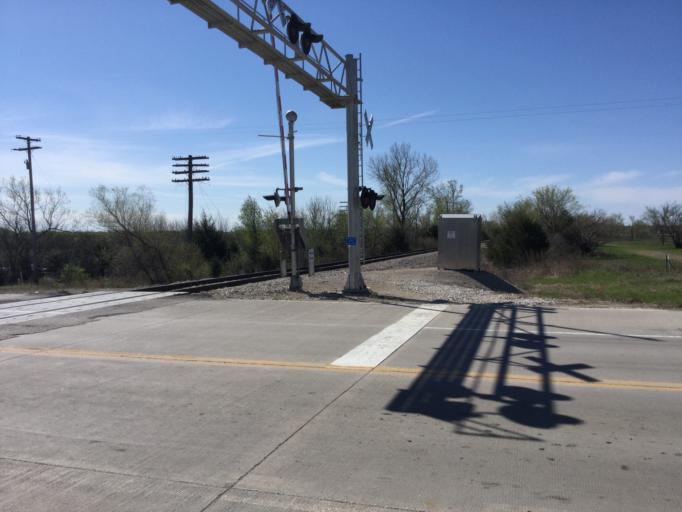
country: US
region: Kansas
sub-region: Neosho County
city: Chanute
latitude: 37.5289
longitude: -95.4705
